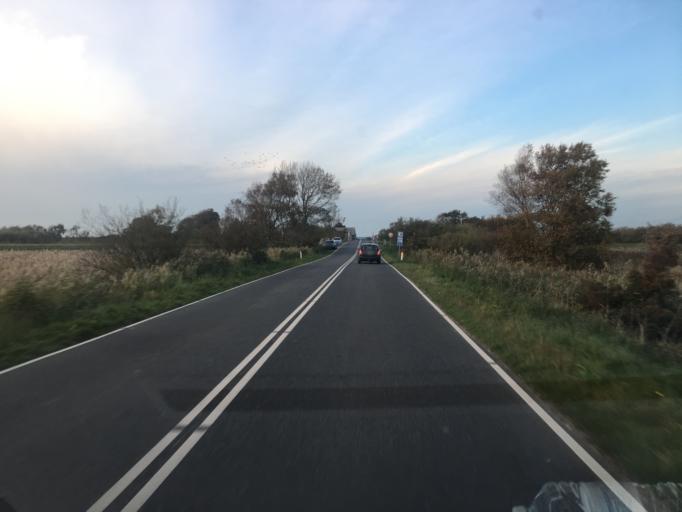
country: DE
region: Schleswig-Holstein
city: Aventoft
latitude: 54.9108
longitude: 8.8332
